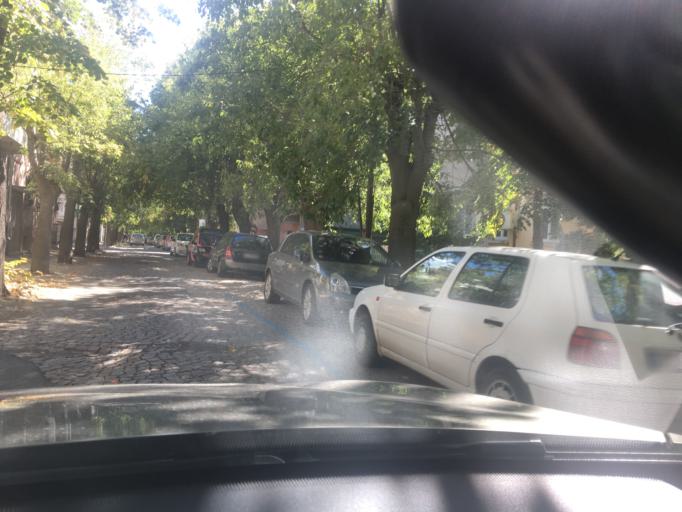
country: BG
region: Burgas
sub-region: Obshtina Burgas
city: Burgas
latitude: 42.4998
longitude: 27.4767
